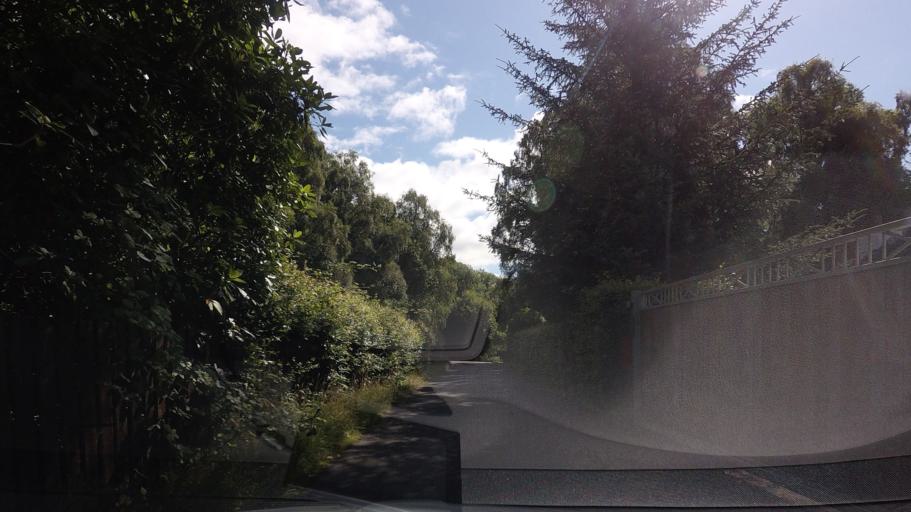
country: GB
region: Scotland
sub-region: Stirling
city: Killearn
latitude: 56.0643
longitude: -4.4682
